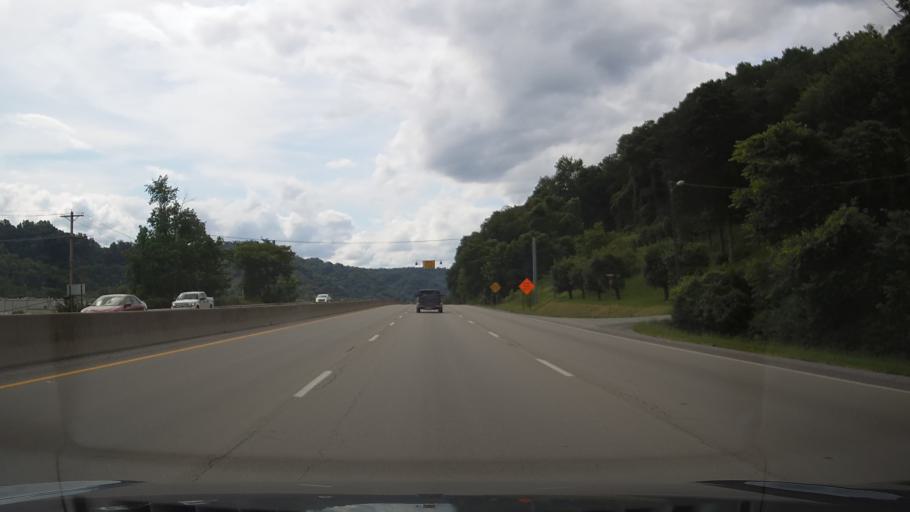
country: US
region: Kentucky
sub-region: Pike County
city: Coal Run Village
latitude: 37.5132
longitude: -82.5555
